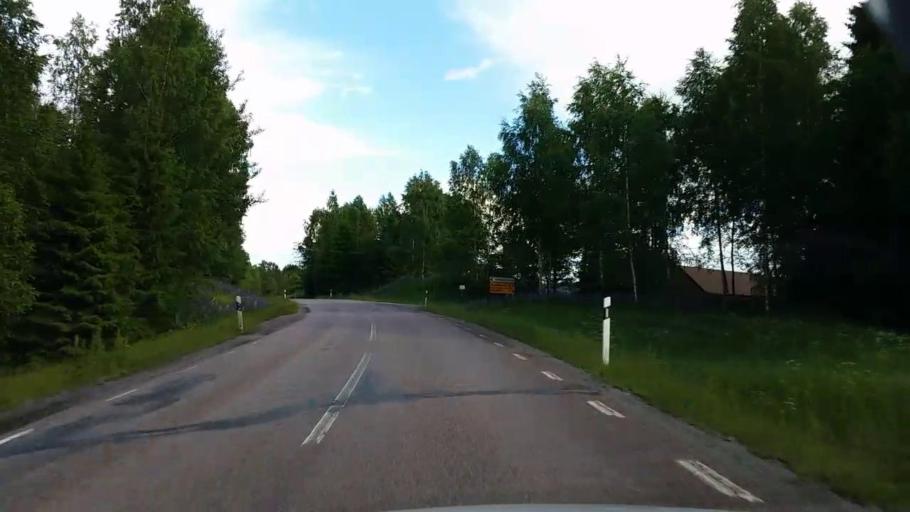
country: SE
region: Vaestmanland
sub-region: Fagersta Kommun
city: Fagersta
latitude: 59.9530
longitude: 15.7864
